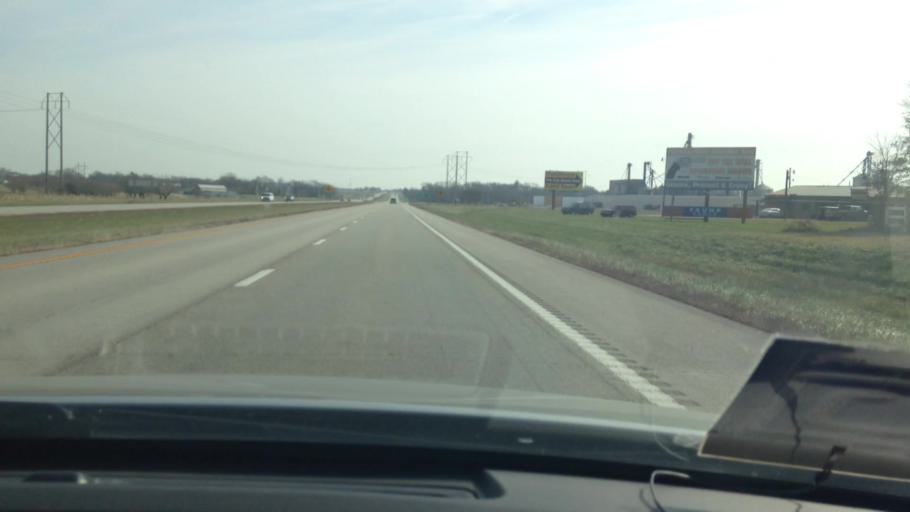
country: US
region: Missouri
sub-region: Cass County
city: Garden City
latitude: 38.5969
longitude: -94.2526
